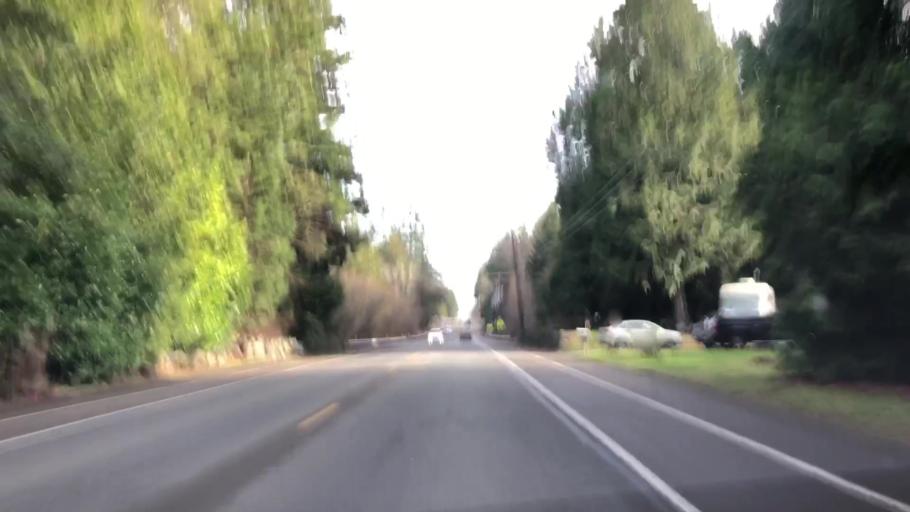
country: US
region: Washington
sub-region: Kitsap County
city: Kingston
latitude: 47.7949
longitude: -122.5316
